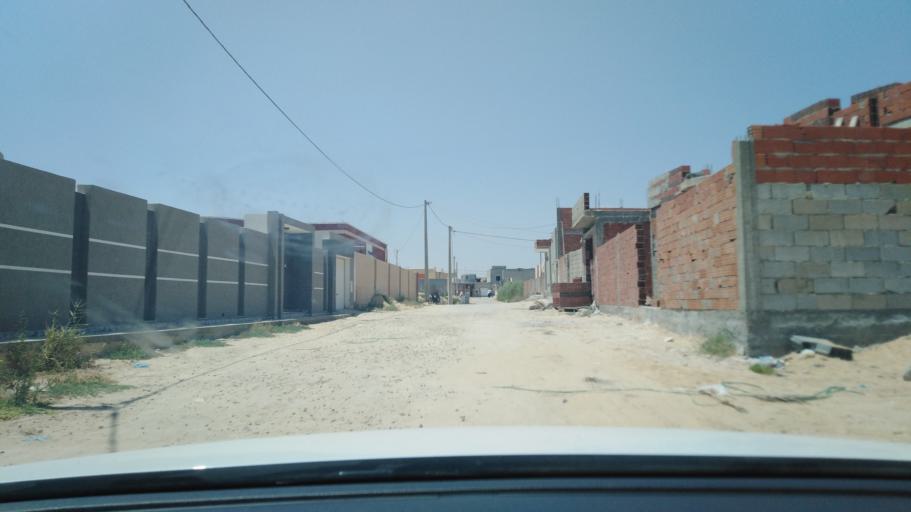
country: TN
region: Qabis
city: Gabes
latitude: 33.9474
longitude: 10.0738
